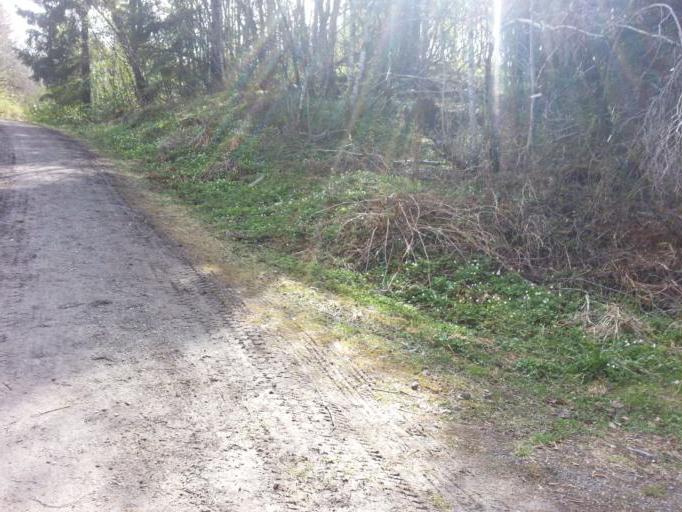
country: NO
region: Sor-Trondelag
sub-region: Trondheim
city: Trondheim
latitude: 63.3961
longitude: 10.3494
